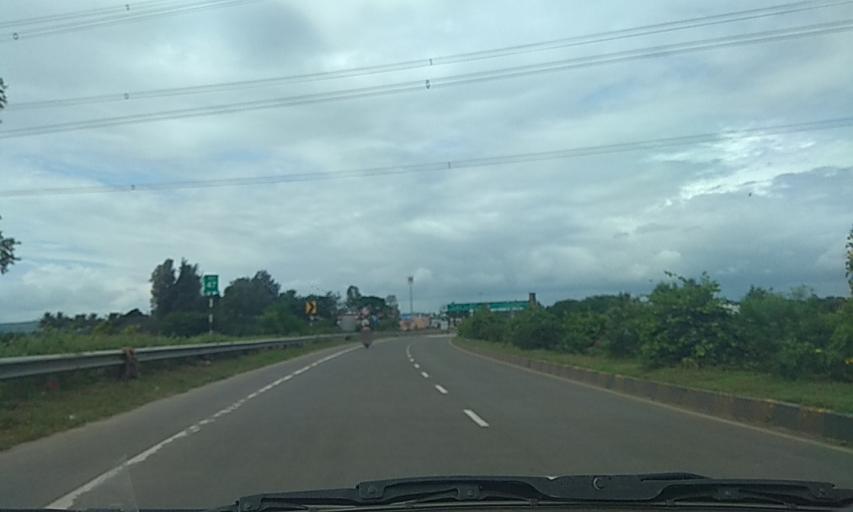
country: IN
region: Maharashtra
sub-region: Kolhapur
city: Kagal
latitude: 16.5570
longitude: 74.3168
